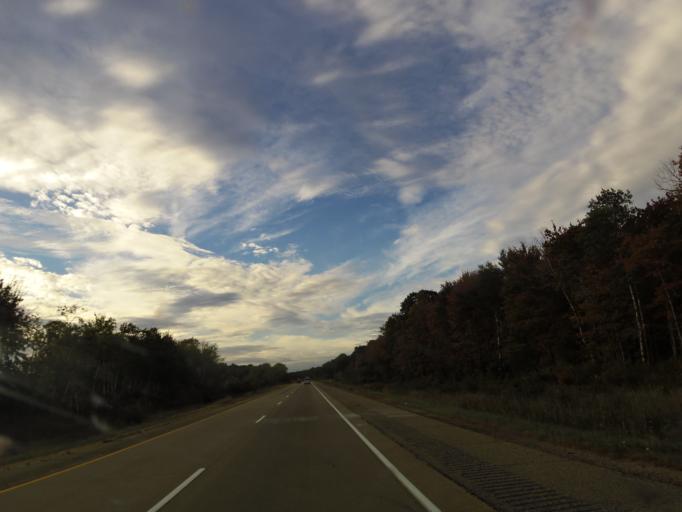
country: US
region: Wisconsin
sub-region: Columbia County
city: Wisconsin Dells
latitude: 43.6860
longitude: -89.8424
